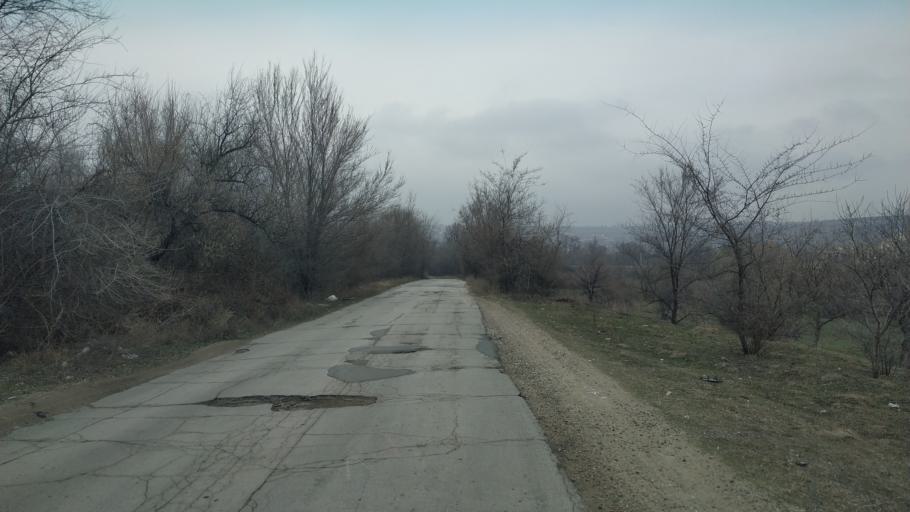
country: MD
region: Chisinau
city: Singera
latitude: 46.9226
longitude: 29.0048
